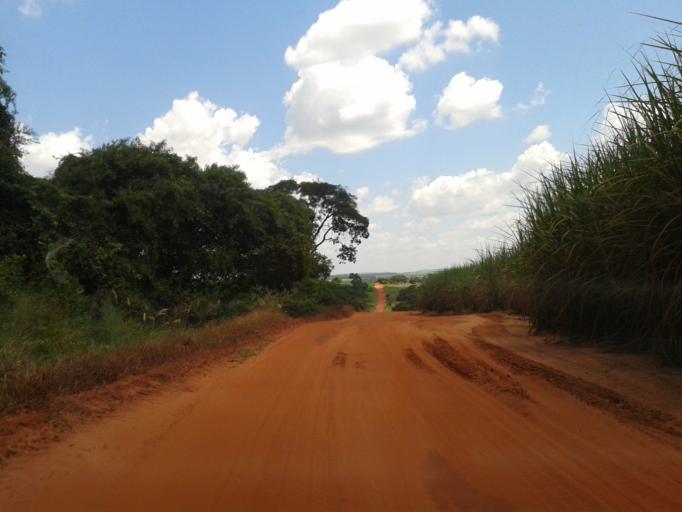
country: BR
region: Minas Gerais
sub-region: Ituiutaba
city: Ituiutaba
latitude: -19.0156
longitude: -49.6833
